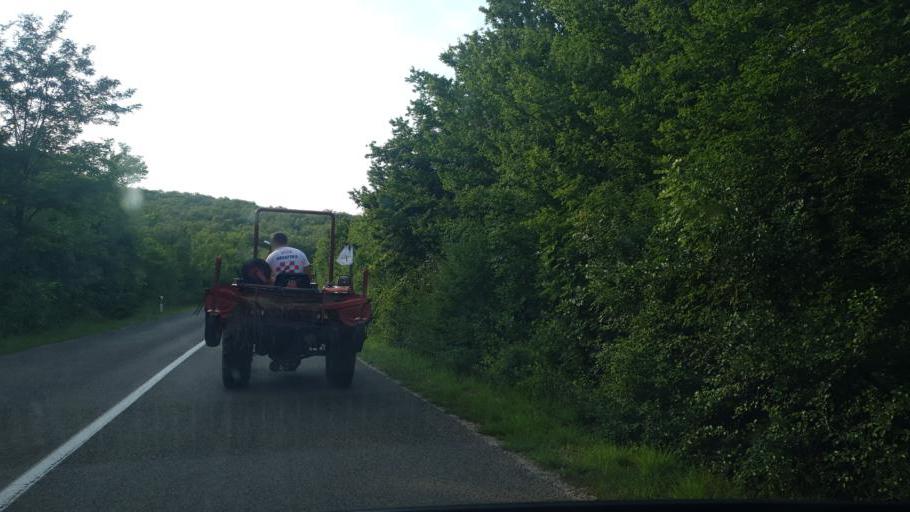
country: HR
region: Primorsko-Goranska
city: Njivice
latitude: 45.1422
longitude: 14.5838
